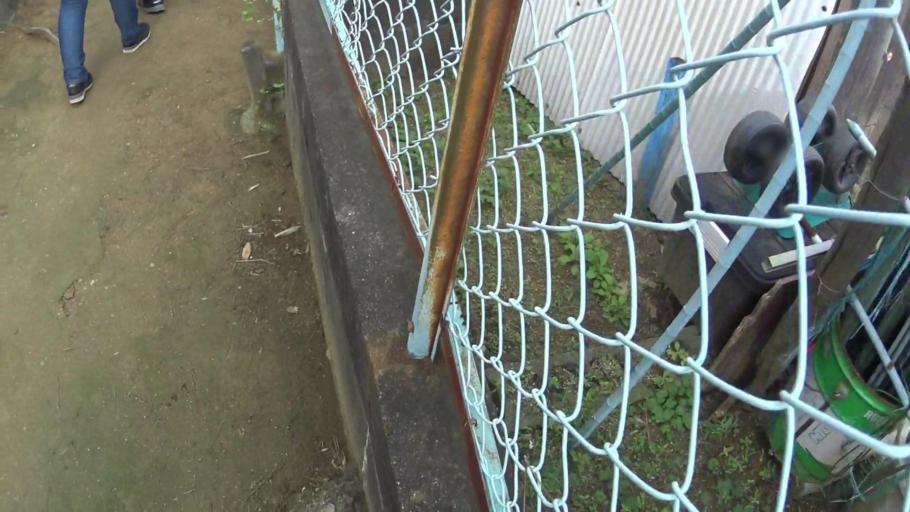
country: JP
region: Osaka
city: Kashihara
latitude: 34.5651
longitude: 135.5955
